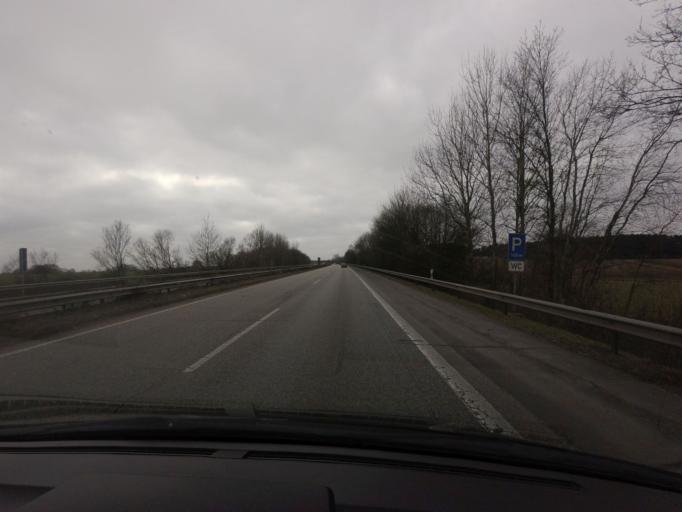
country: DE
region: Lower Saxony
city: Buchholz in der Nordheide
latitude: 53.3958
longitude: 9.8908
